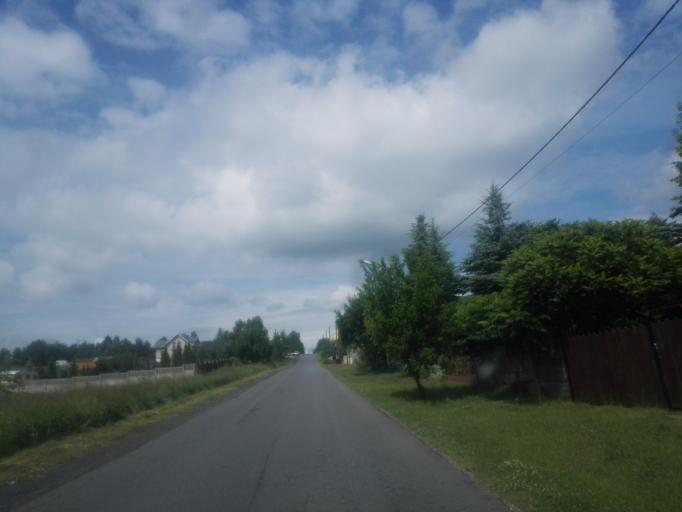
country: PL
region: Silesian Voivodeship
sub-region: Powiat myszkowski
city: Choron
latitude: 50.7070
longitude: 19.2934
